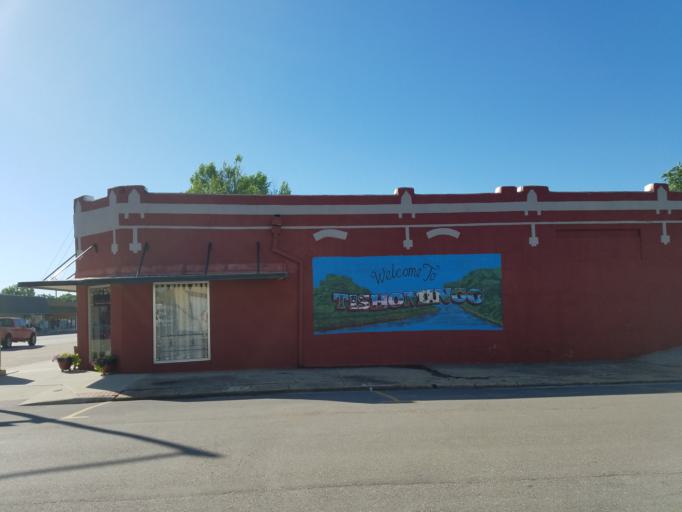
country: US
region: Oklahoma
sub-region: Johnston County
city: Tishomingo
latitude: 34.2363
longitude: -96.6803
